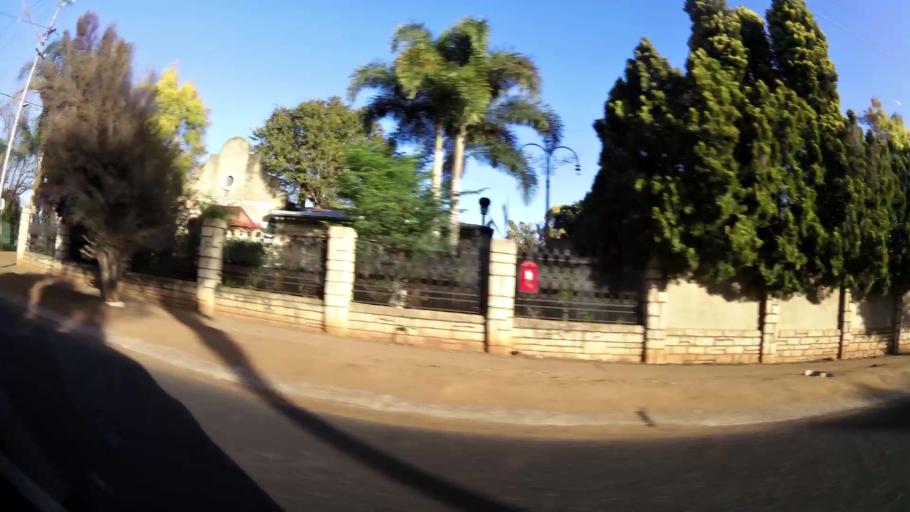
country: ZA
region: Gauteng
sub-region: City of Tshwane Metropolitan Municipality
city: Pretoria
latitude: -25.7049
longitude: 28.2242
